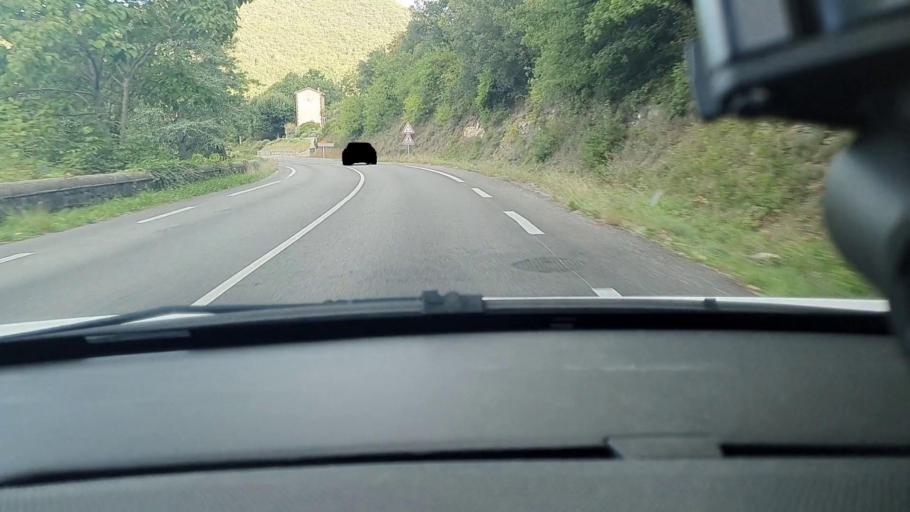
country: FR
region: Languedoc-Roussillon
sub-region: Departement du Gard
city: Besseges
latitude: 44.2834
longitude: 4.1273
